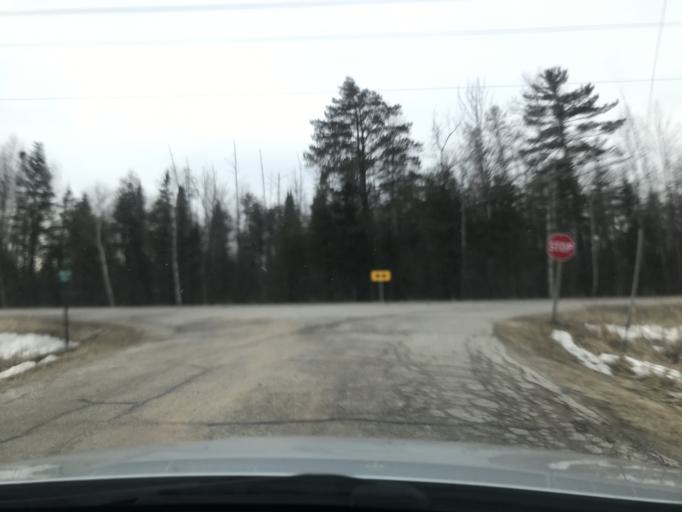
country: US
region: Wisconsin
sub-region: Oconto County
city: Oconto
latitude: 45.1090
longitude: -88.0083
